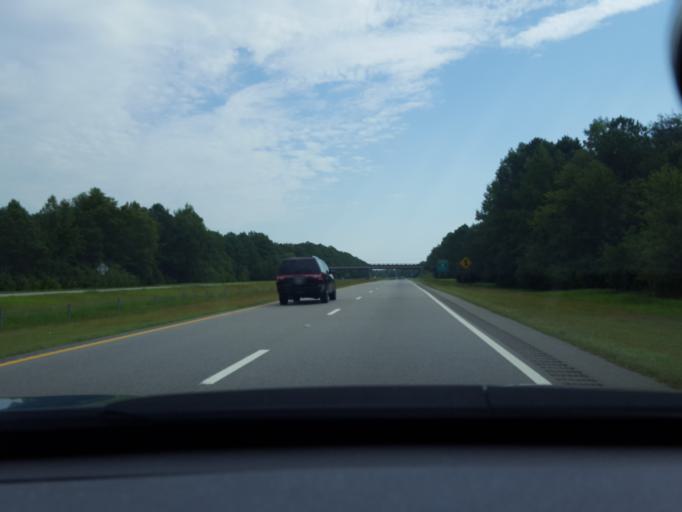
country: US
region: North Carolina
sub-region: Chowan County
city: Edenton
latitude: 36.0689
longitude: -76.6341
